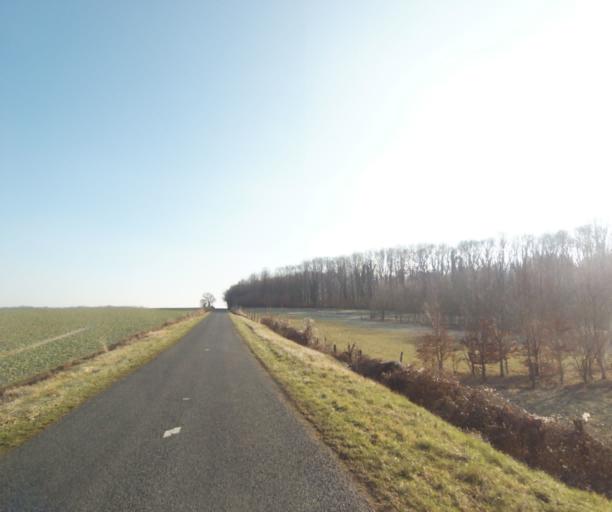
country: FR
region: Champagne-Ardenne
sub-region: Departement de la Haute-Marne
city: Chevillon
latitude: 48.4909
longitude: 5.0754
